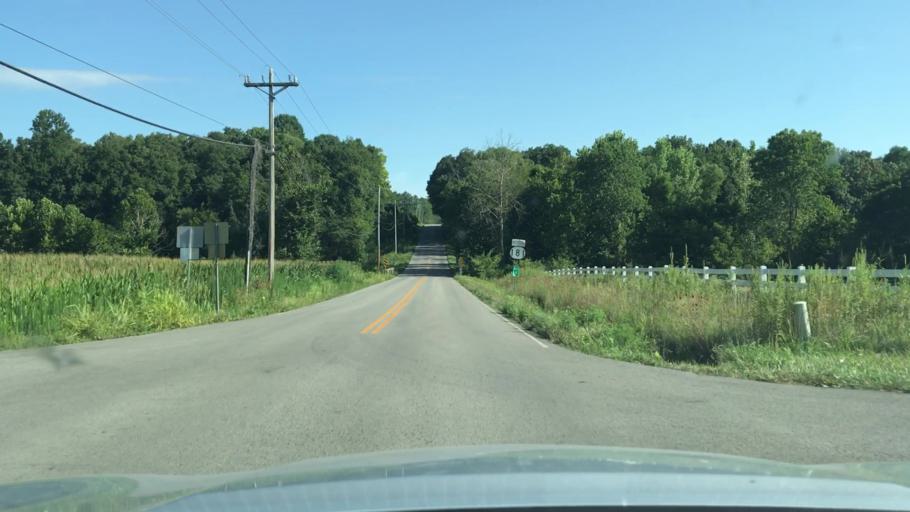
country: US
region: Kentucky
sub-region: Muhlenberg County
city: Greenville
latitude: 37.1016
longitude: -87.1265
